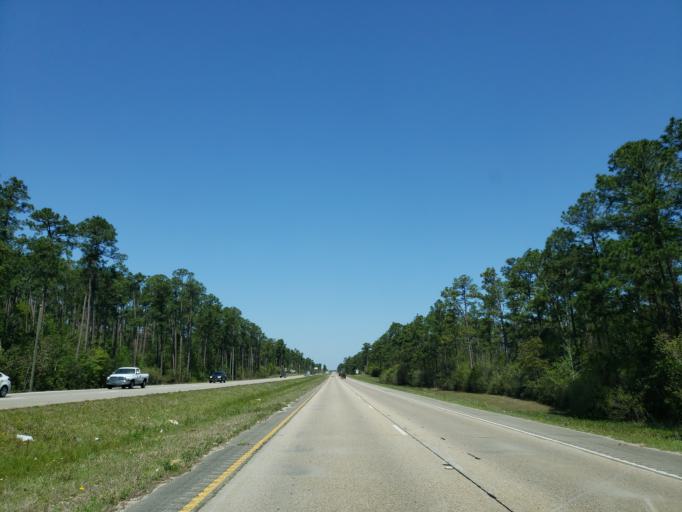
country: US
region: Mississippi
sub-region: Harrison County
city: Lyman
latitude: 30.5297
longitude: -89.1099
